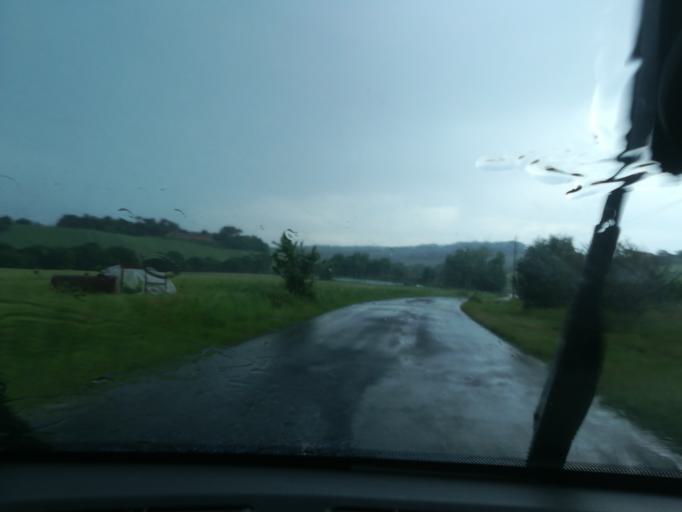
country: IT
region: The Marches
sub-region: Provincia di Macerata
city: Passo di Treia
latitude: 43.3049
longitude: 13.3441
